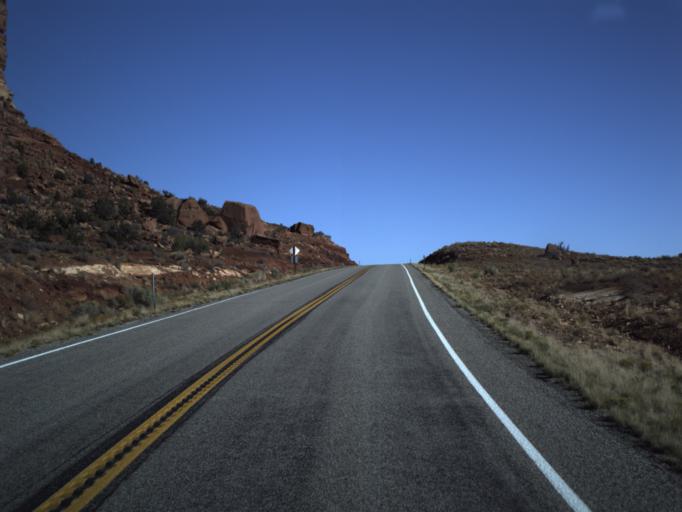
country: US
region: Utah
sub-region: San Juan County
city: Blanding
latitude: 37.7442
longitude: -110.2808
